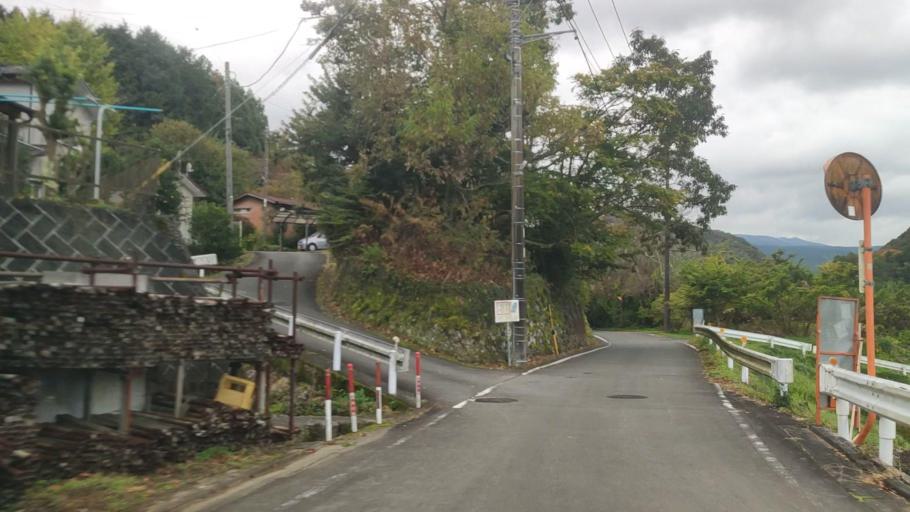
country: JP
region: Shizuoka
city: Ito
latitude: 34.9408
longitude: 138.9984
